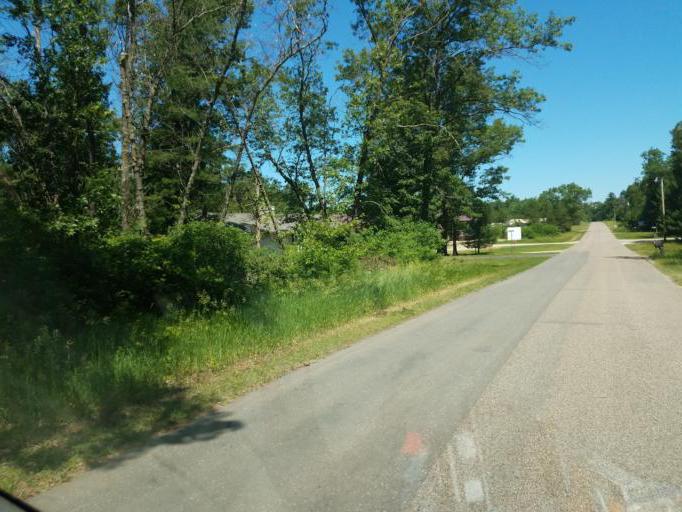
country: US
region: Wisconsin
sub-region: Adams County
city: Friendship
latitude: 44.0029
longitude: -89.9557
